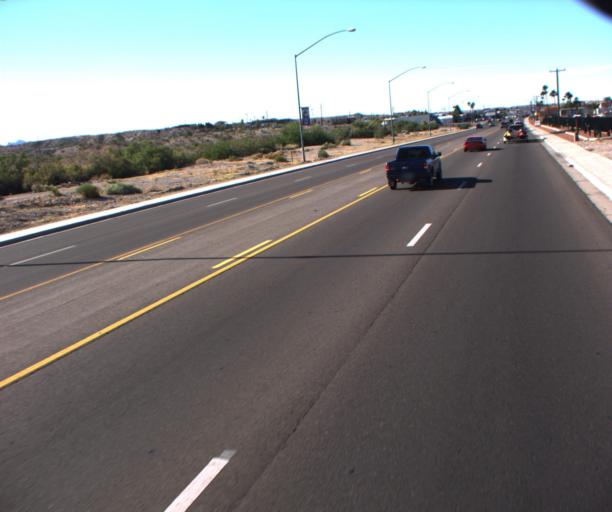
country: US
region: Arizona
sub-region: Mohave County
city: Bullhead City
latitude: 35.1566
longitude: -114.5671
